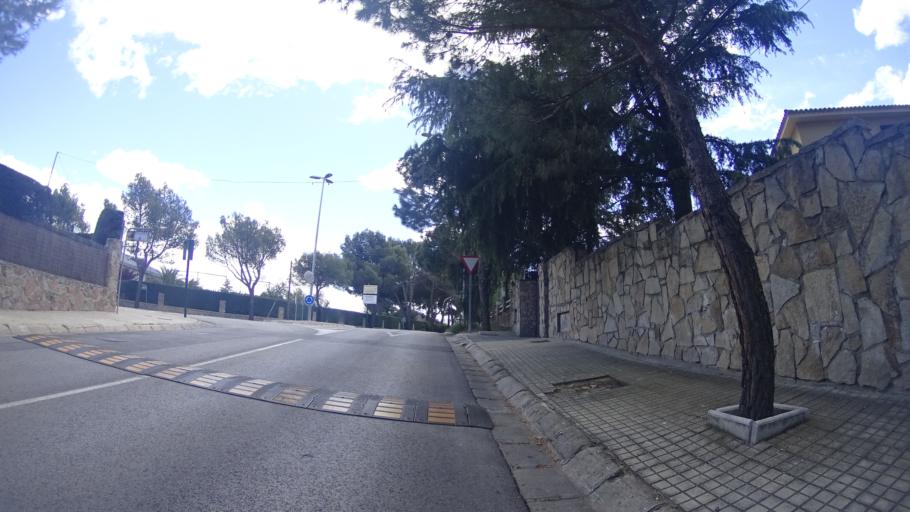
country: ES
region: Madrid
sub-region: Provincia de Madrid
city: Villaviciosa de Odon
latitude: 40.3715
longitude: -3.9251
